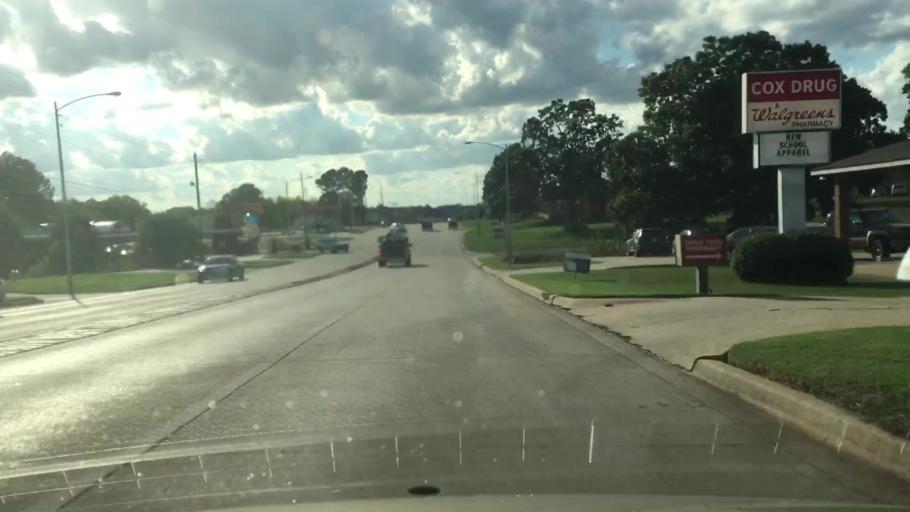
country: US
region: Oklahoma
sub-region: Cherokee County
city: Tahlequah
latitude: 35.9154
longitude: -94.9519
